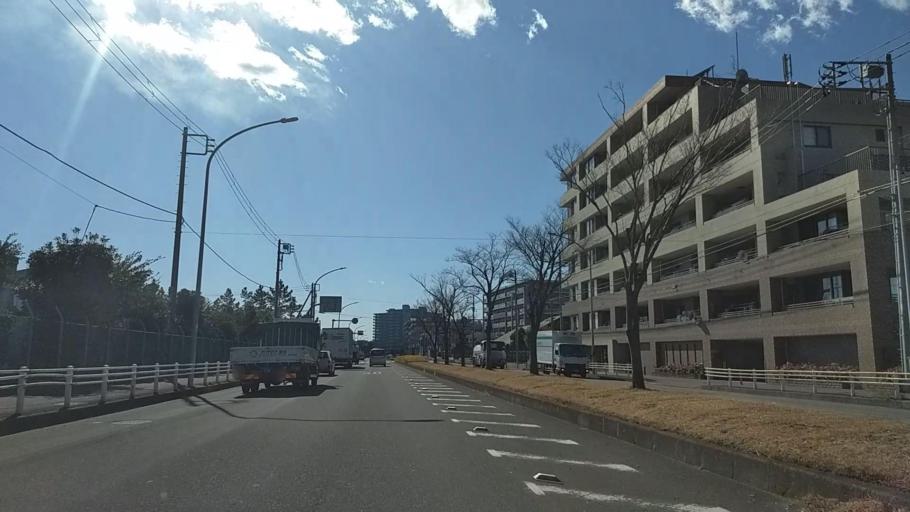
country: JP
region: Kanagawa
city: Yokosuka
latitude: 35.3447
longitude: 139.6389
